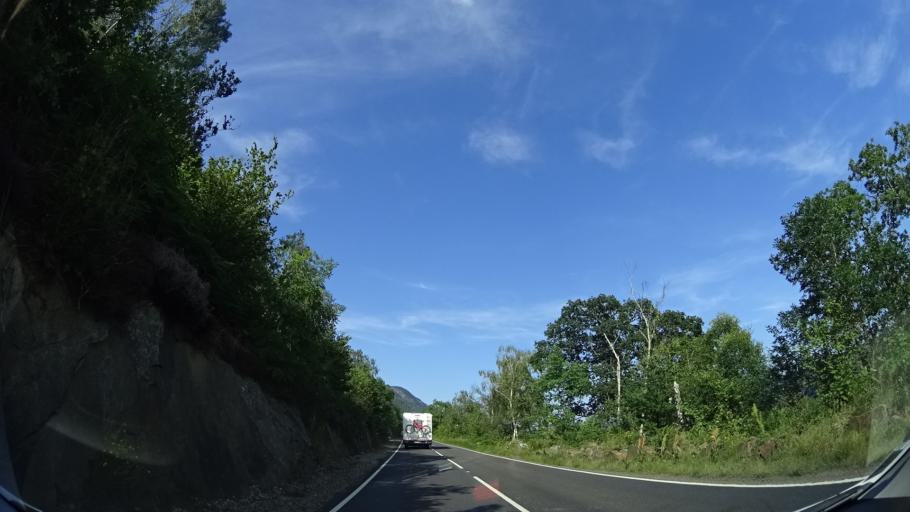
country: GB
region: Scotland
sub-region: Highland
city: Beauly
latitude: 57.3704
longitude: -4.3869
